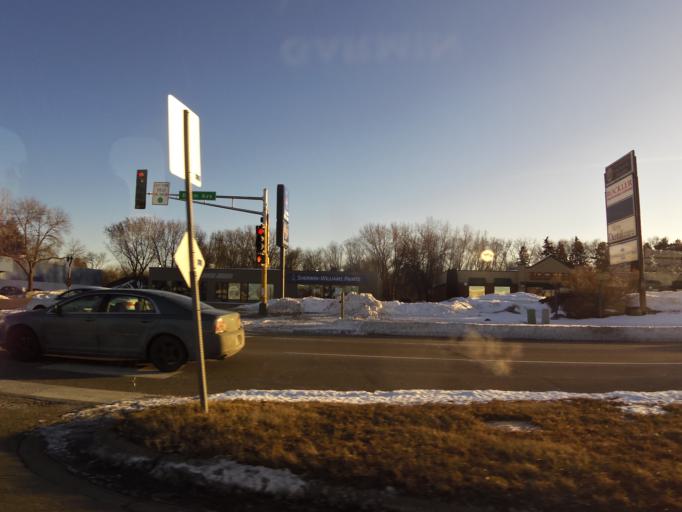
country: US
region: Minnesota
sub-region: Ramsey County
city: North Saint Paul
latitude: 45.0281
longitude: -93.0206
